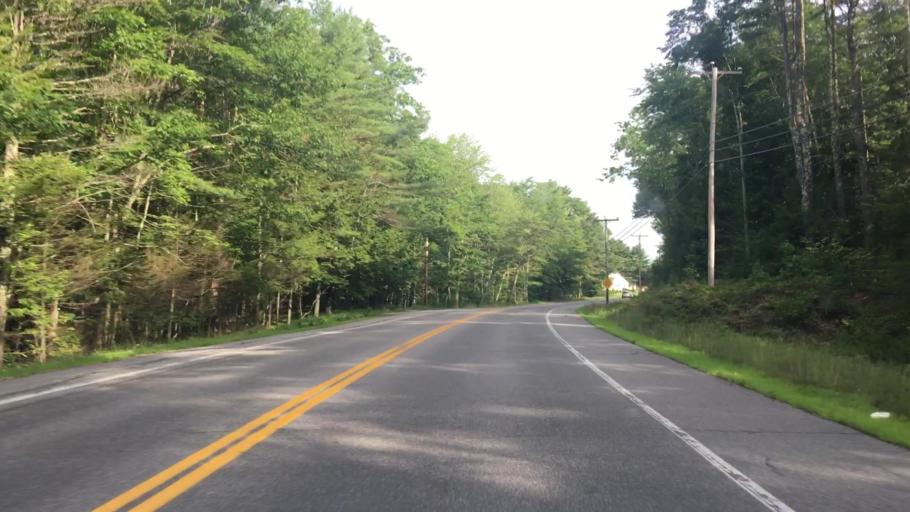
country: US
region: Maine
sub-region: York County
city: Limington
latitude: 43.7400
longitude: -70.6737
